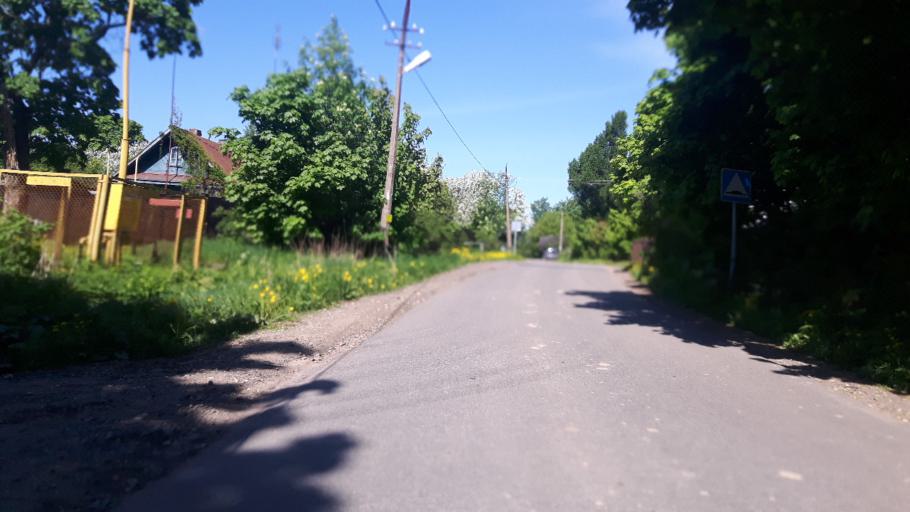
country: RU
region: Leningrad
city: Lebyazh'ye
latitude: 59.9685
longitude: 29.3932
